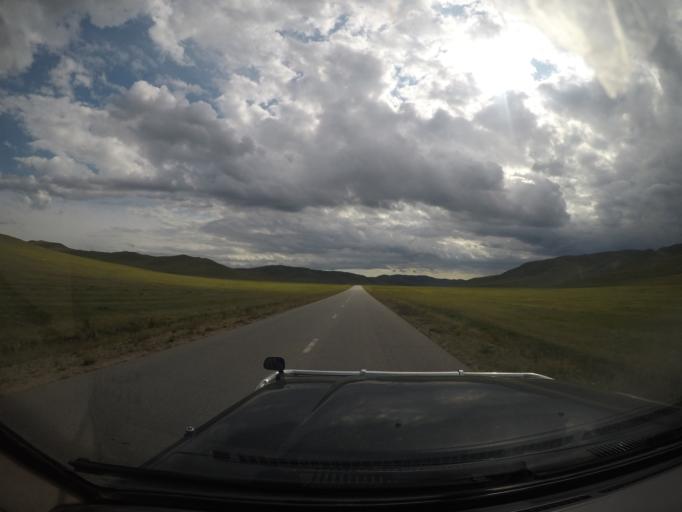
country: MN
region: Central Aimak
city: Bayandelger
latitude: 47.7146
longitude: 108.5742
